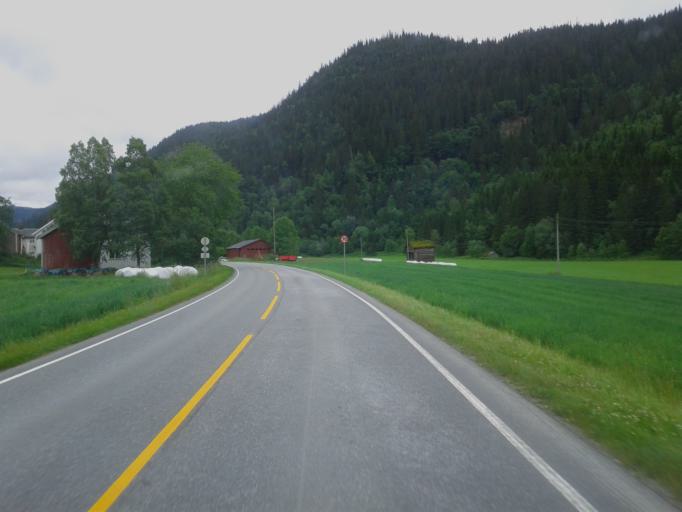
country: NO
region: Sor-Trondelag
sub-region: Midtre Gauldal
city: Storen
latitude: 63.0135
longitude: 10.3626
